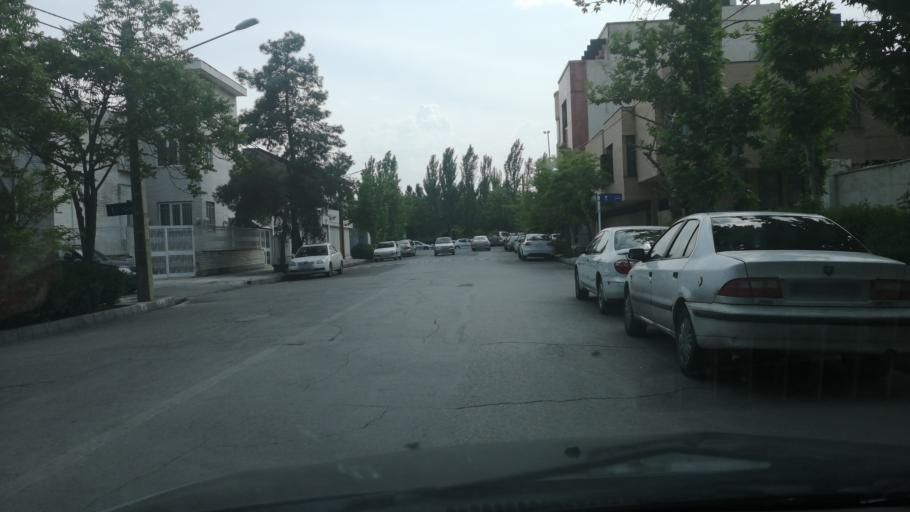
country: IR
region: Razavi Khorasan
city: Mashhad
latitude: 36.3070
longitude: 59.5548
